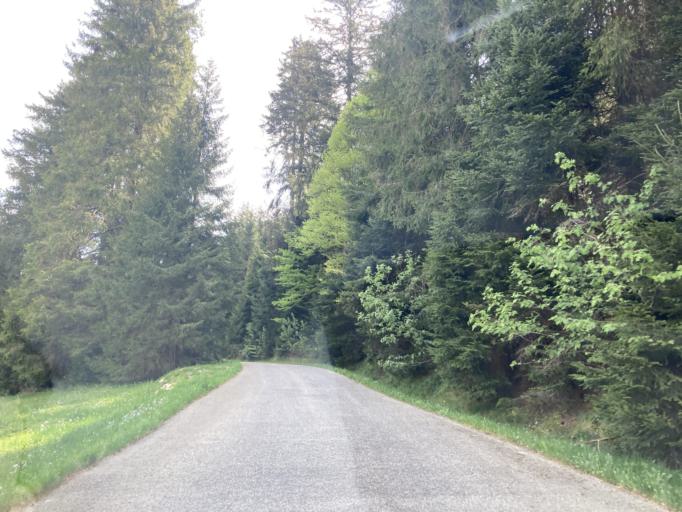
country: DE
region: Baden-Wuerttemberg
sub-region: Karlsruhe Region
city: Biberach
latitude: 48.5294
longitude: 8.2844
